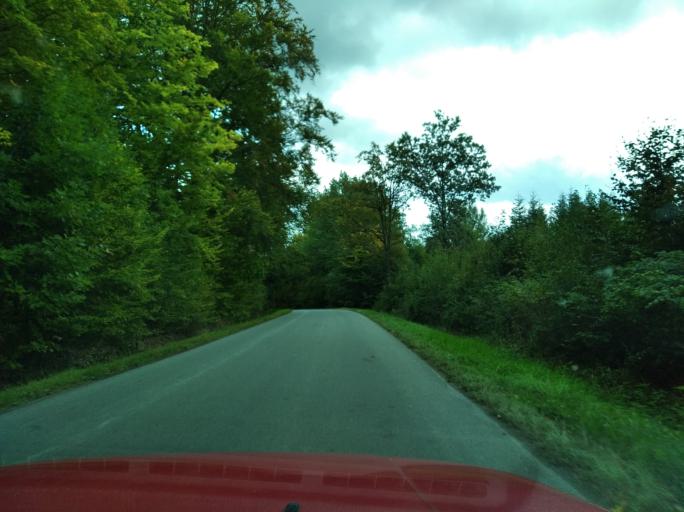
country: PL
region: Subcarpathian Voivodeship
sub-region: Powiat rzeszowski
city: Straszydle
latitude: 49.9311
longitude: 21.9992
